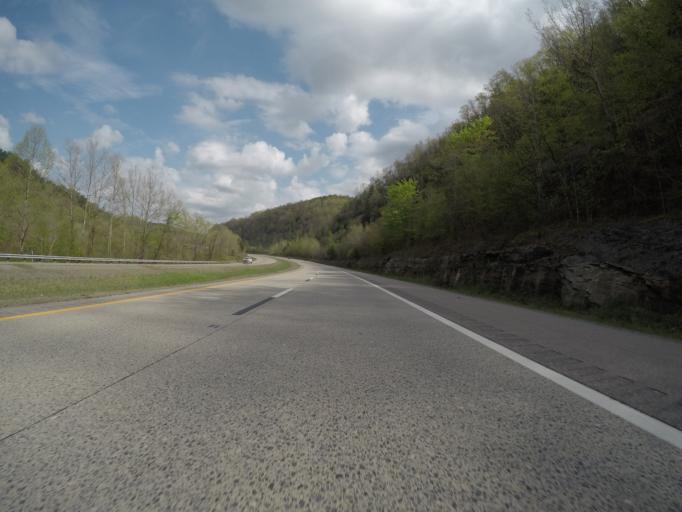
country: US
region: West Virginia
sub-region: Kanawha County
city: Alum Creek
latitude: 38.2104
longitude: -81.8297
